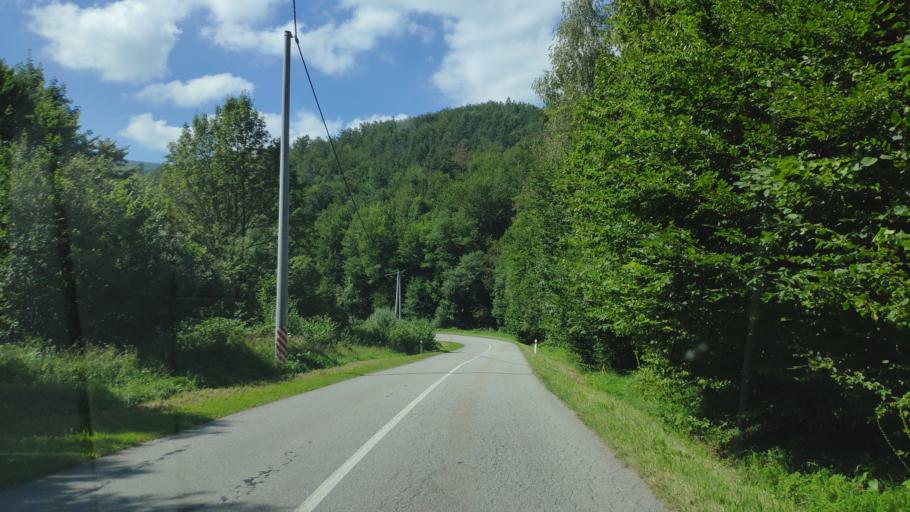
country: PL
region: Subcarpathian Voivodeship
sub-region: Powiat leski
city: Cisna
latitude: 49.0735
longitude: 22.3758
